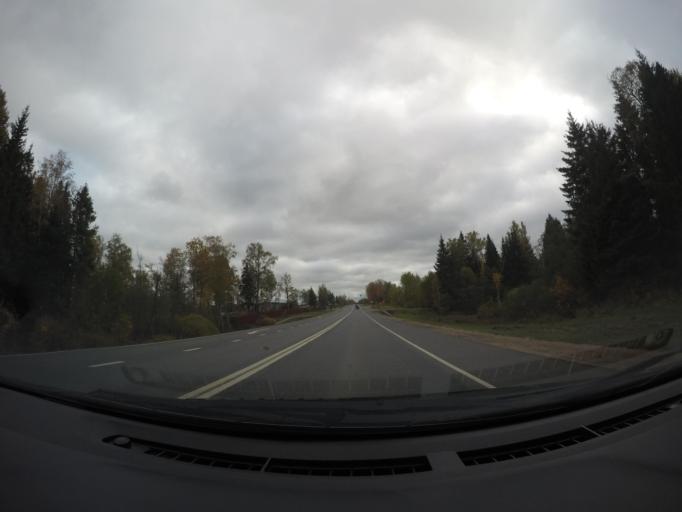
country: RU
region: Moskovskaya
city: Dorokhovo
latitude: 55.5992
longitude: 36.3598
